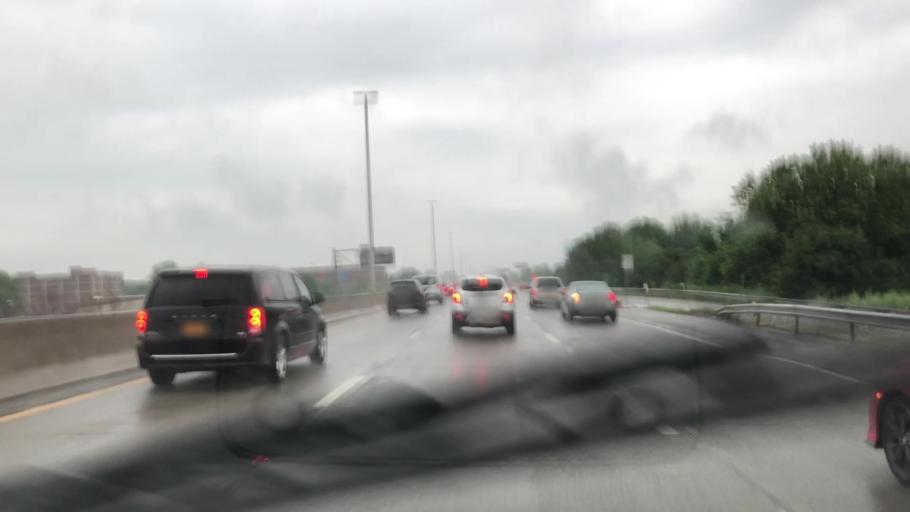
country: US
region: New York
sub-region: Erie County
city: West Seneca
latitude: 42.8678
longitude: -78.8303
